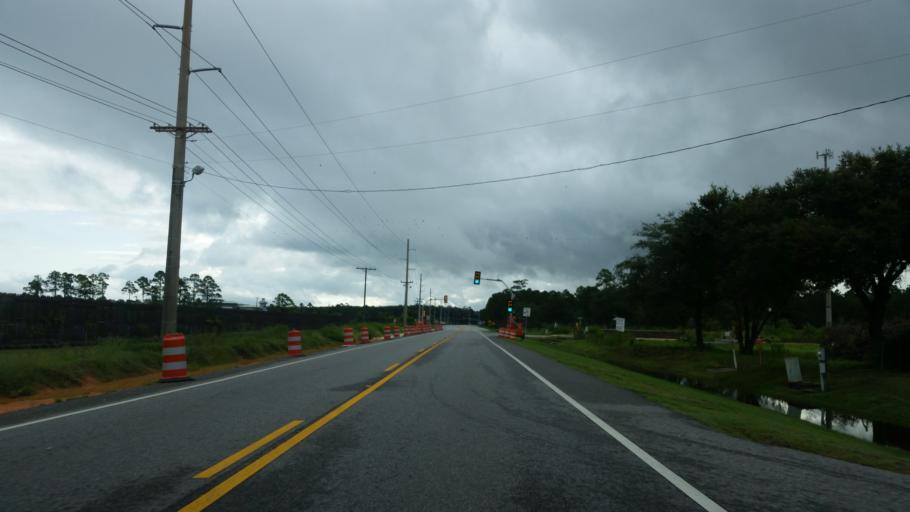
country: US
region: Alabama
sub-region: Baldwin County
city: Orange Beach
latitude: 30.2888
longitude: -87.6359
